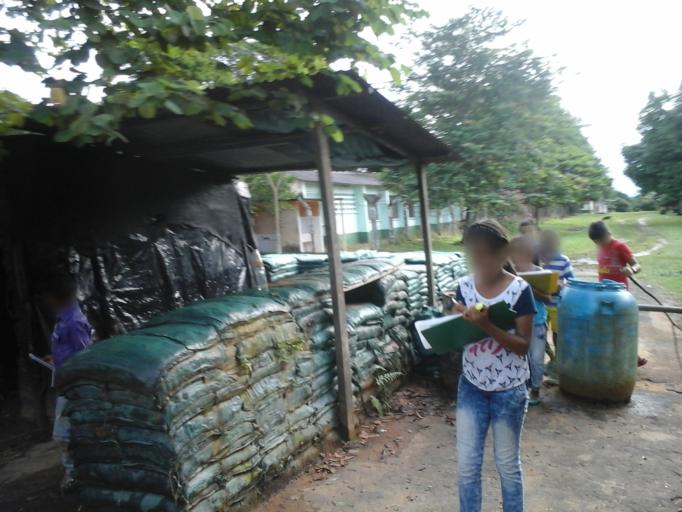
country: CO
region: Caqueta
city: El Doncello
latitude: 1.6136
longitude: -74.9964
